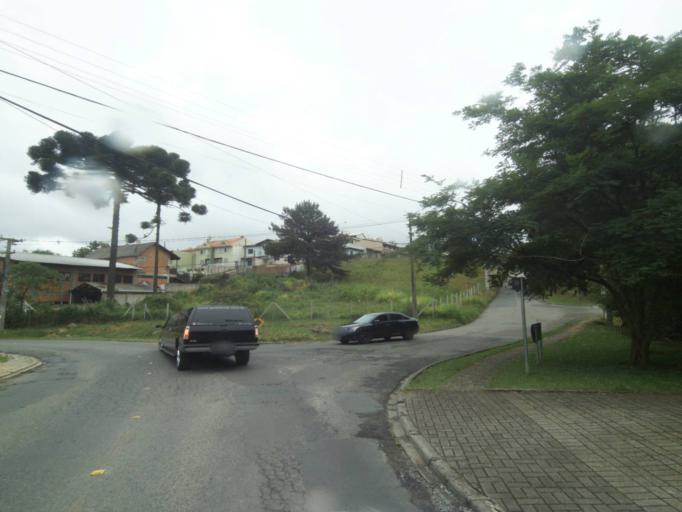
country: BR
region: Parana
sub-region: Curitiba
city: Curitiba
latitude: -25.4237
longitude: -49.3397
